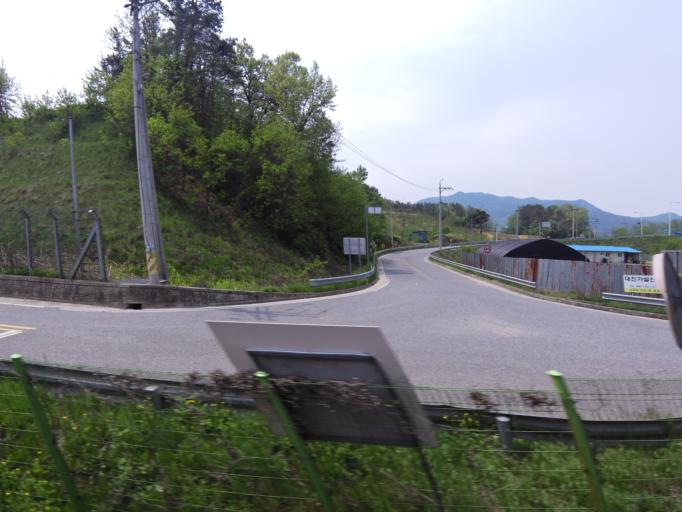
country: KR
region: Chungcheongbuk-do
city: Okcheon
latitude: 36.2776
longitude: 127.5800
